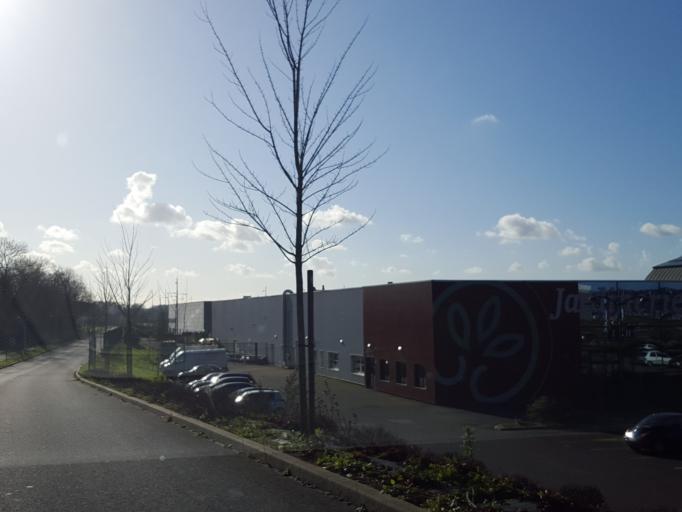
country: FR
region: Pays de la Loire
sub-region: Departement de la Vendee
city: La Roche-sur-Yon
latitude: 46.6428
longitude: -1.4347
